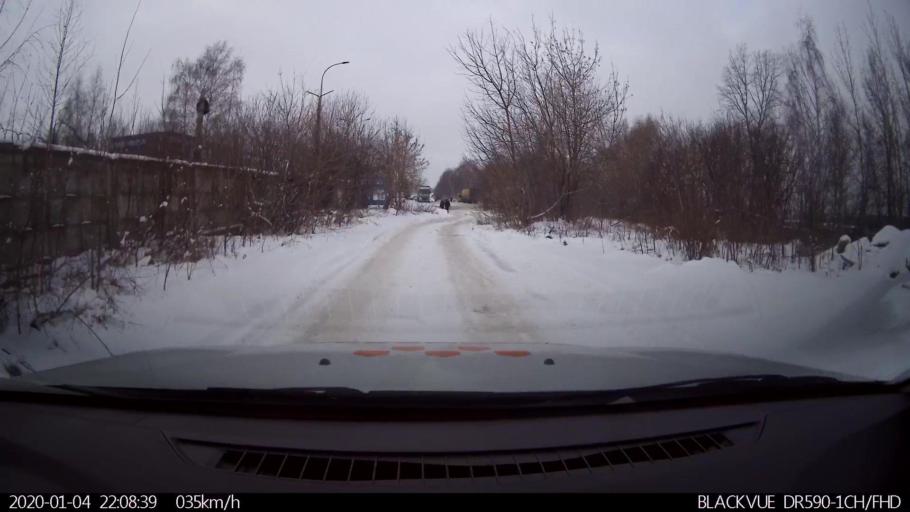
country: RU
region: Nizjnij Novgorod
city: Afonino
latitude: 56.2363
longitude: 44.0145
